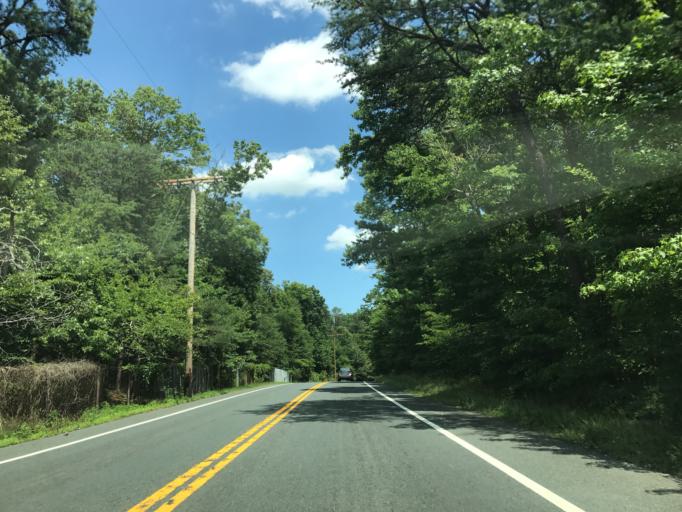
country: US
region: Maryland
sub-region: Prince George's County
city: South Laurel
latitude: 39.0467
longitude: -76.8238
